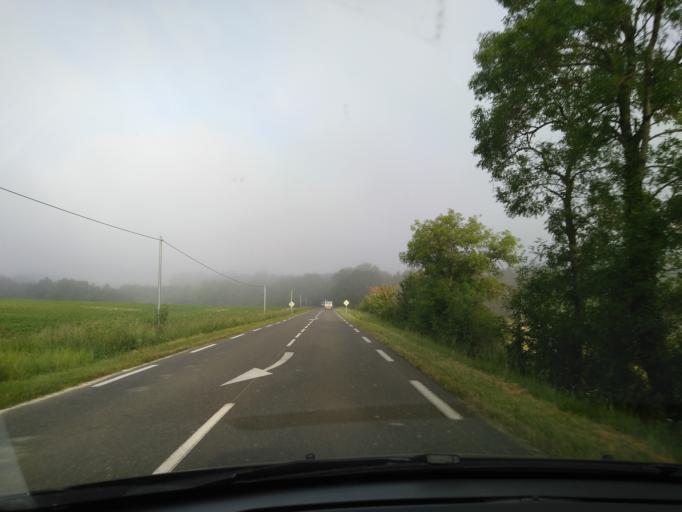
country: FR
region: Midi-Pyrenees
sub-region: Departement du Gers
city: Gondrin
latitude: 43.8783
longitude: 0.1814
